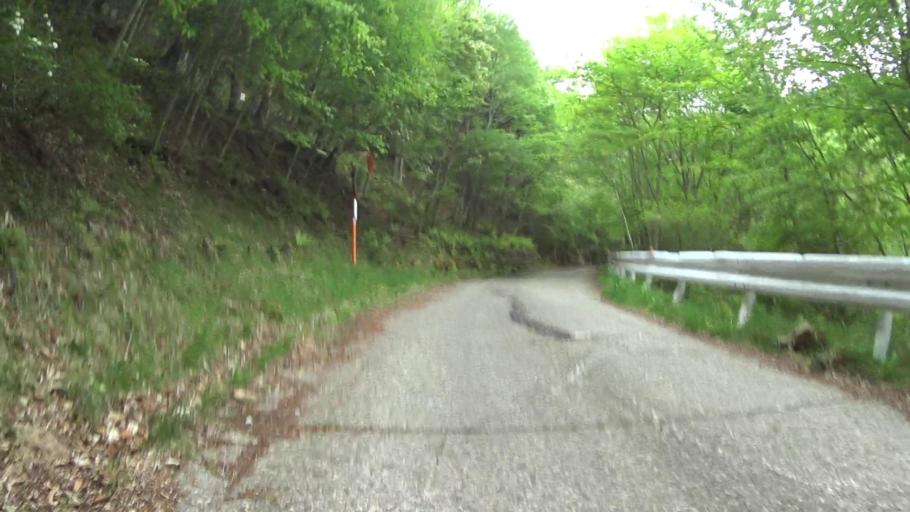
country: JP
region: Yamanashi
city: Kofu-shi
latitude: 35.8453
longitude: 138.5771
